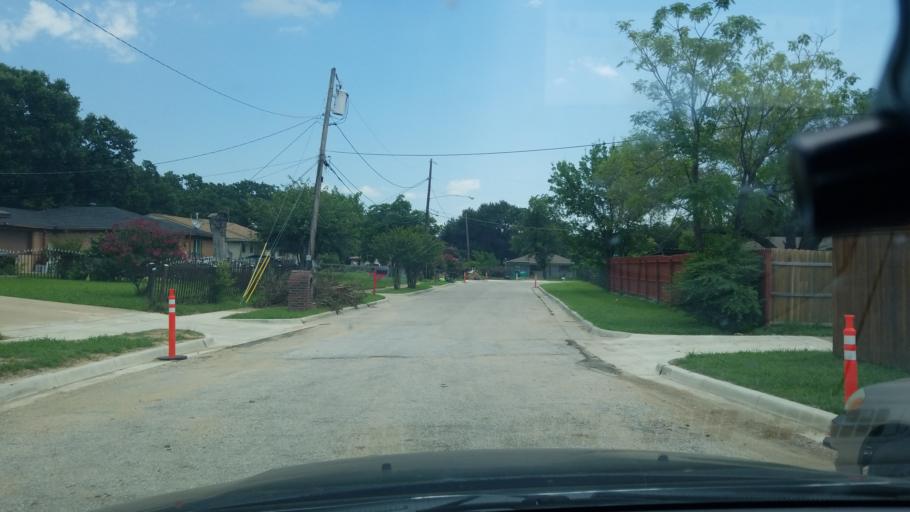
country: US
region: Texas
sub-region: Dallas County
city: Balch Springs
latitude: 32.7240
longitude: -96.6593
